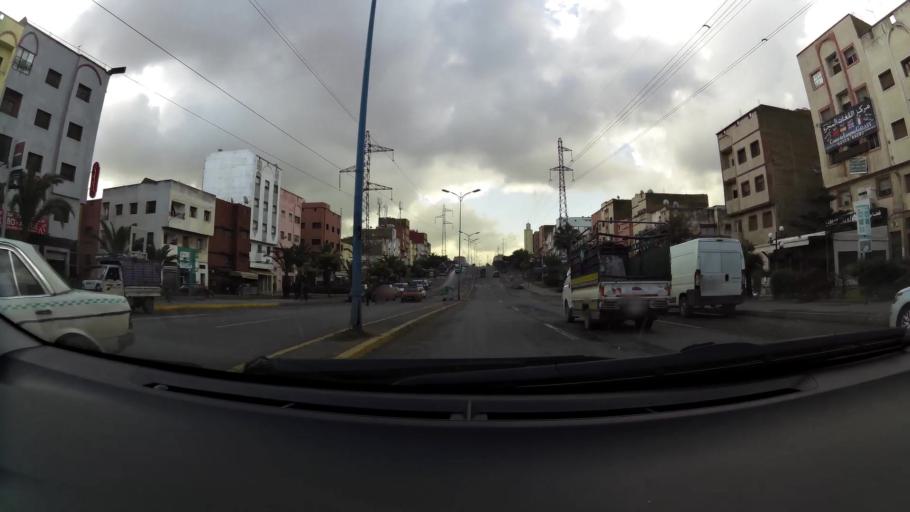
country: MA
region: Grand Casablanca
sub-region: Mediouna
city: Tit Mellil
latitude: 33.5771
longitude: -7.5408
